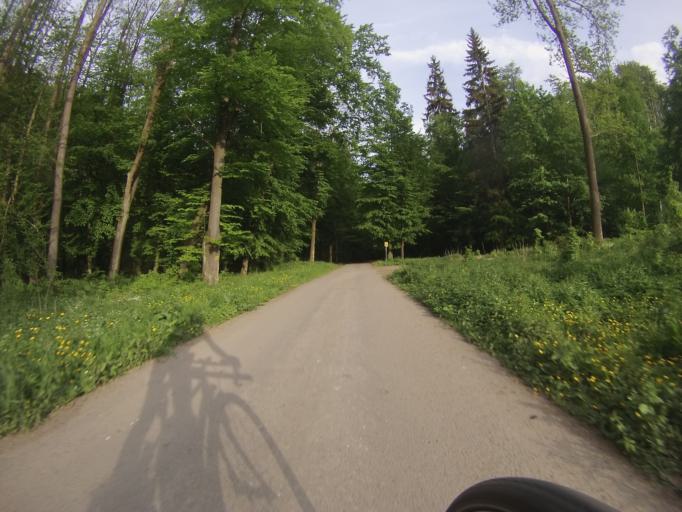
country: CZ
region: Olomoucky
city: Pteni
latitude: 49.4790
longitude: 16.9213
